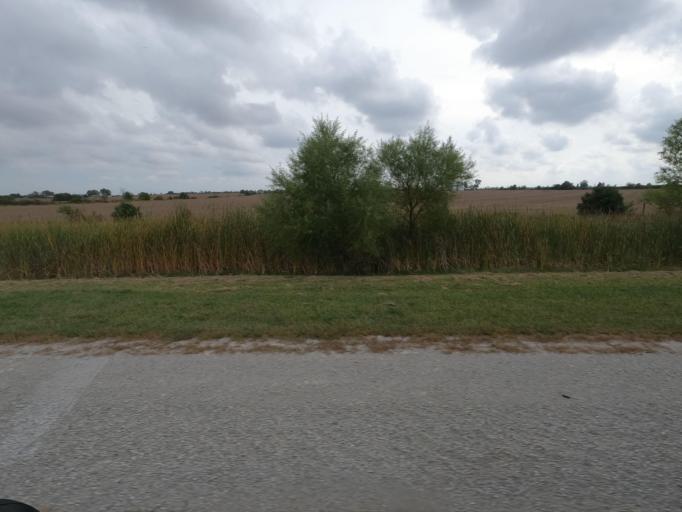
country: US
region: Iowa
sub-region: Wapello County
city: Ottumwa
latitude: 41.0019
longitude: -92.2528
